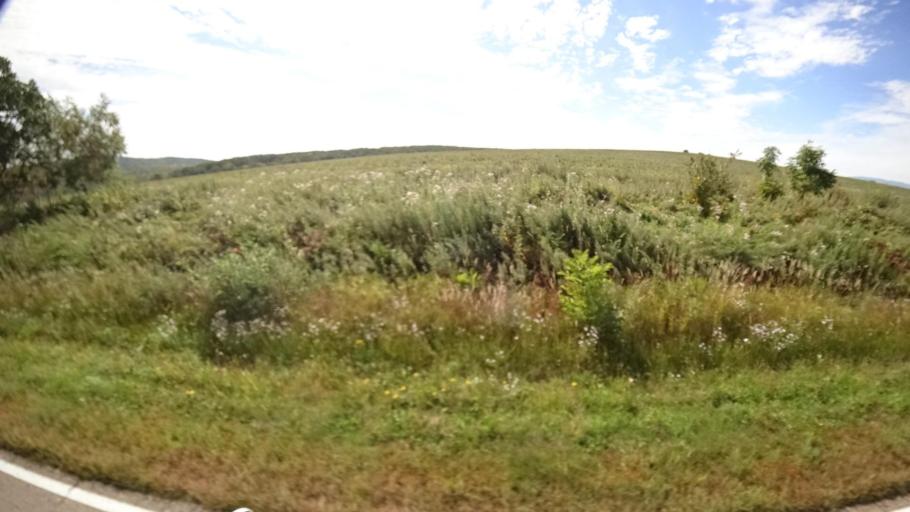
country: RU
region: Primorskiy
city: Yakovlevka
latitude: 44.4138
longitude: 133.5856
